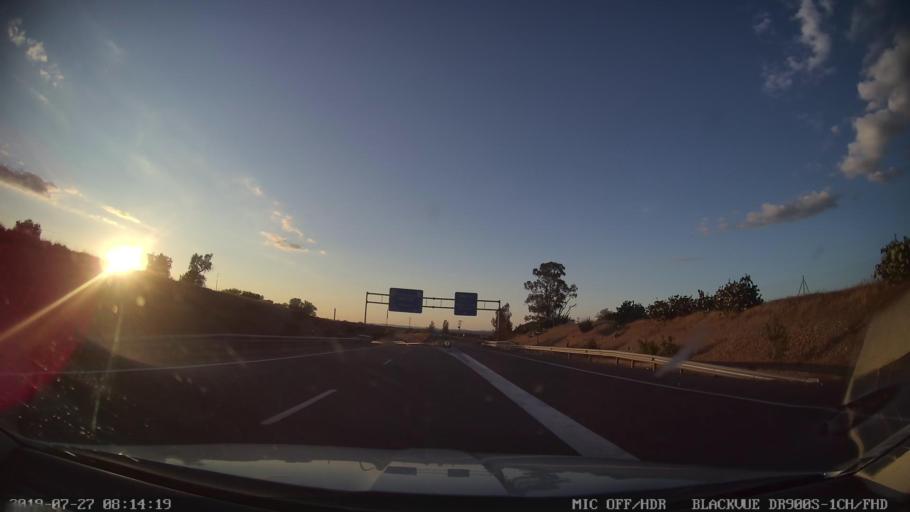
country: ES
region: Extremadura
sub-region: Provincia de Badajoz
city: Calamonte
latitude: 38.9088
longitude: -6.3763
